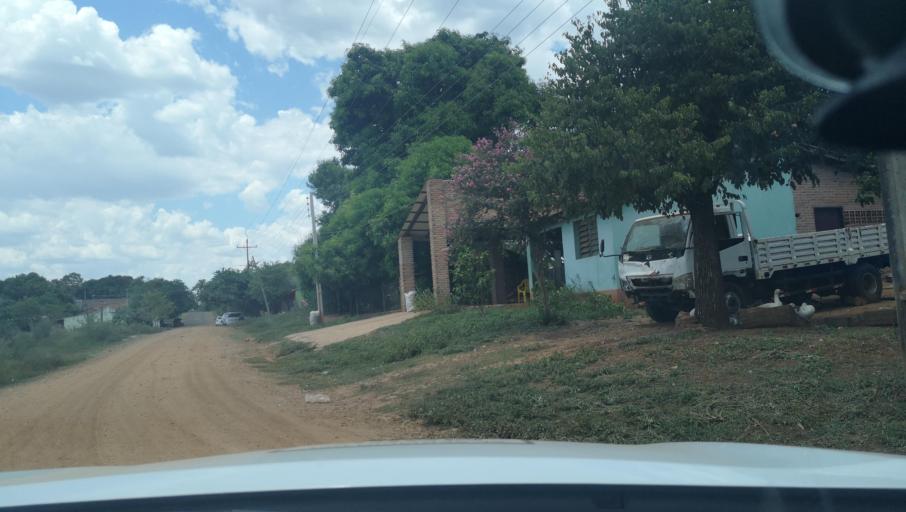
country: PY
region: Itapua
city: Carmen del Parana
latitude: -27.1715
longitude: -56.2484
